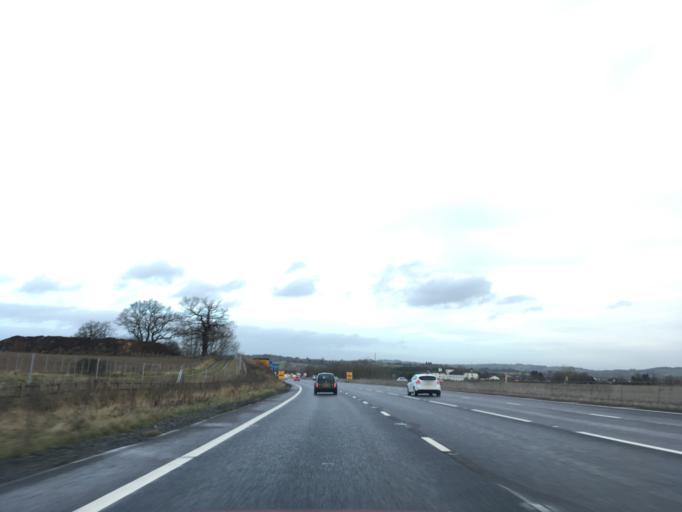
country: GB
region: England
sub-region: Worcestershire
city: Bromsgrove
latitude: 52.3314
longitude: -2.0848
